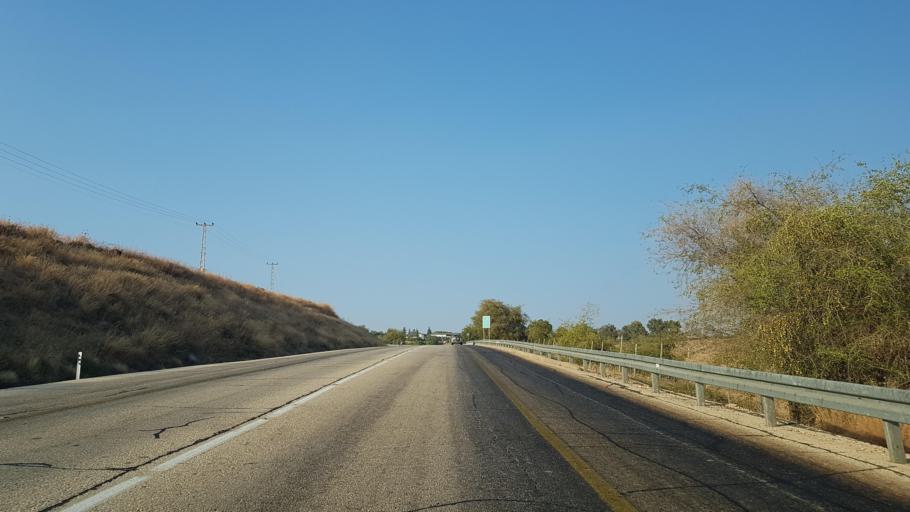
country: SY
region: Quneitra
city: Al Butayhah
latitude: 32.9006
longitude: 35.5969
